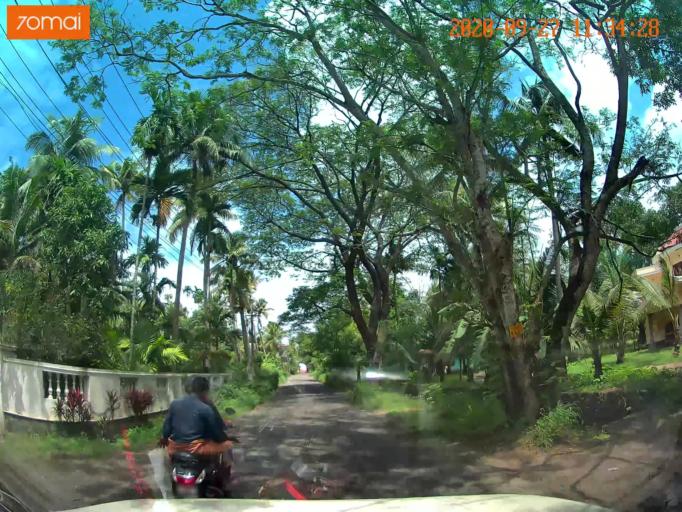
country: IN
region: Kerala
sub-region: Thrissur District
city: Thanniyam
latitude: 10.4369
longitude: 76.1267
